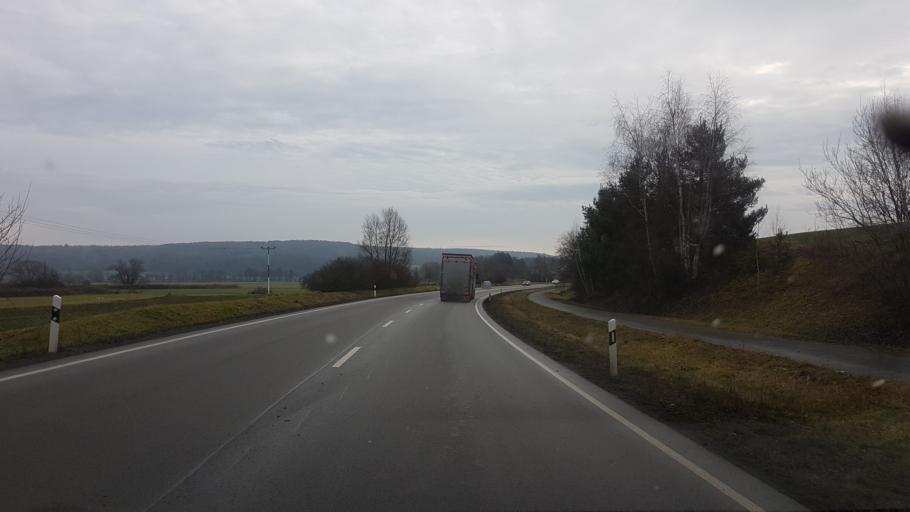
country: DE
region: Bavaria
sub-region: Upper Franconia
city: Gerach
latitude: 50.0389
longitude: 10.8219
